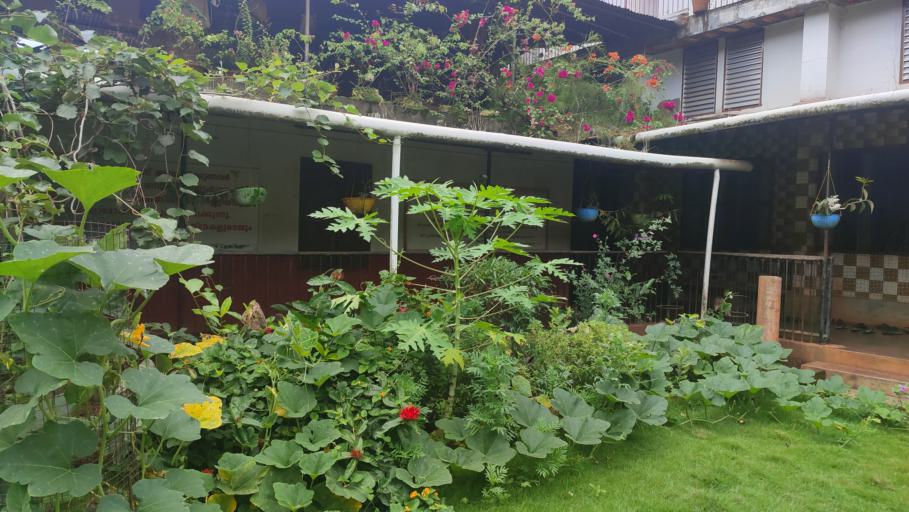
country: IN
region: Karnataka
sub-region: Dakshina Kannada
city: Sulya
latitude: 12.4458
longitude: 75.2451
